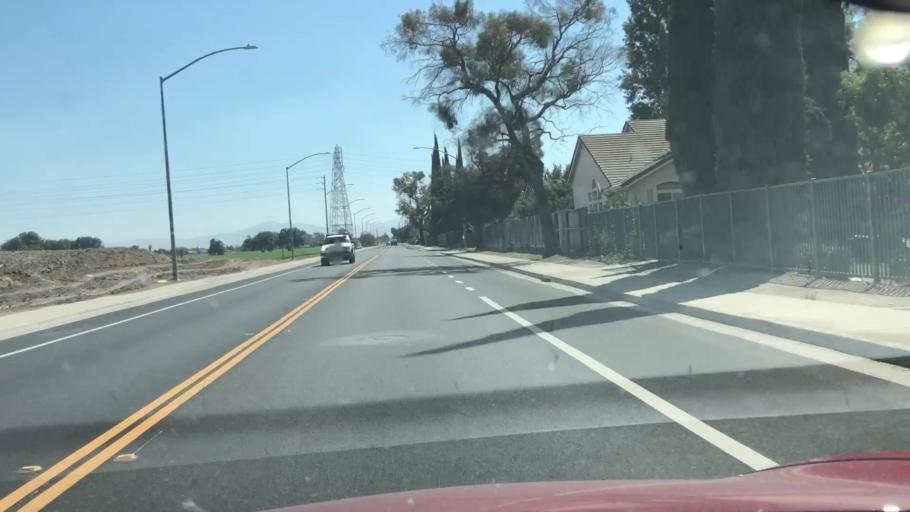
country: US
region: California
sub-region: San Joaquin County
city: Tracy
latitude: 37.7345
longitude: -121.4166
